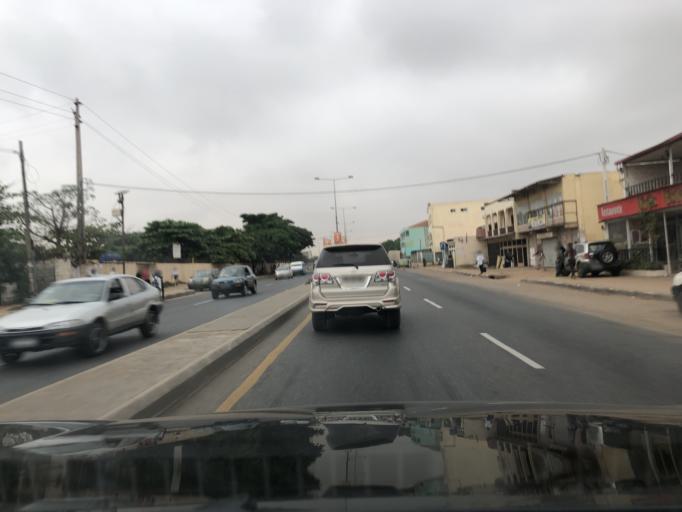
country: AO
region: Luanda
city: Luanda
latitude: -8.8515
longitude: 13.2810
